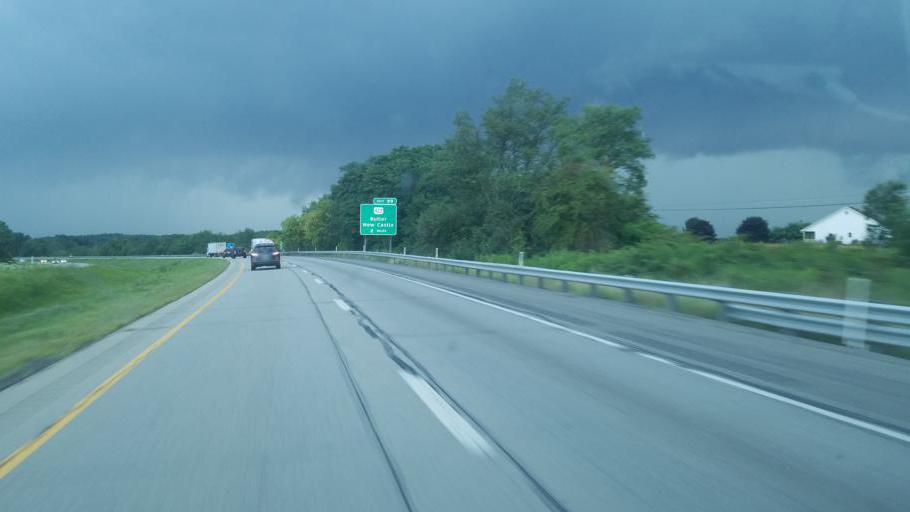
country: US
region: Pennsylvania
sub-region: Butler County
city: Slippery Rock
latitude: 40.9914
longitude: -80.1283
